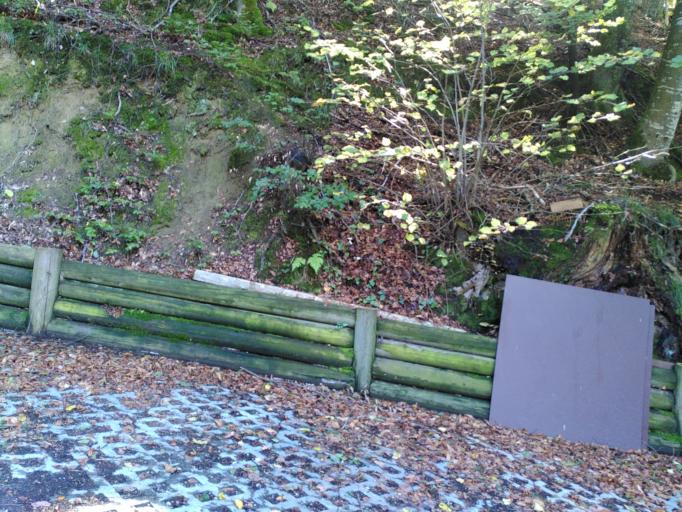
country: CH
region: Bern
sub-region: Oberaargau
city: Seeberg
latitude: 47.1308
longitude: 7.7171
